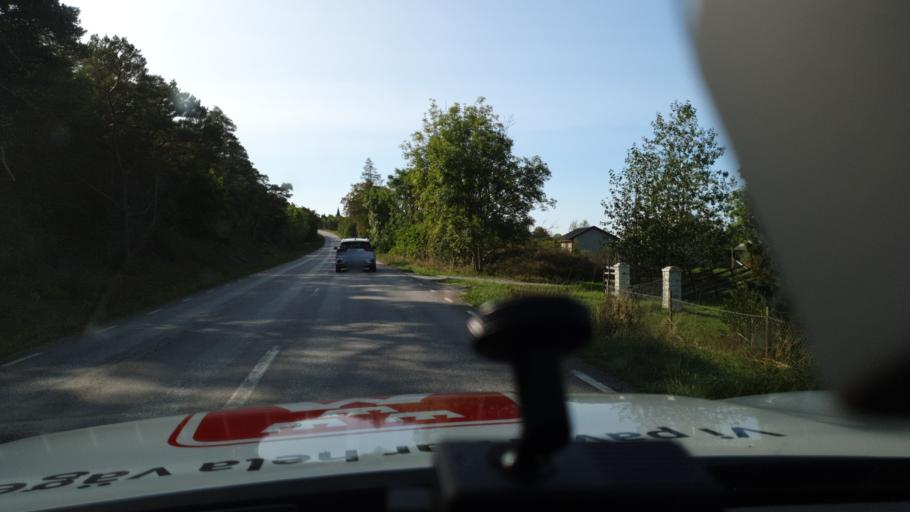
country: SE
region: Gotland
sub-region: Gotland
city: Klintehamn
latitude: 57.3427
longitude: 18.1914
